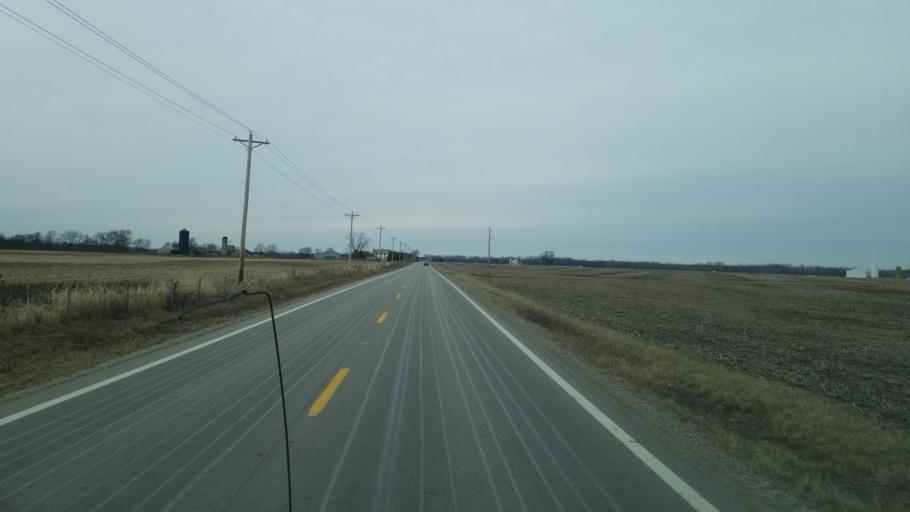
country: US
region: Ohio
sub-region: Pickaway County
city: Circleville
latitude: 39.6030
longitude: -83.0043
